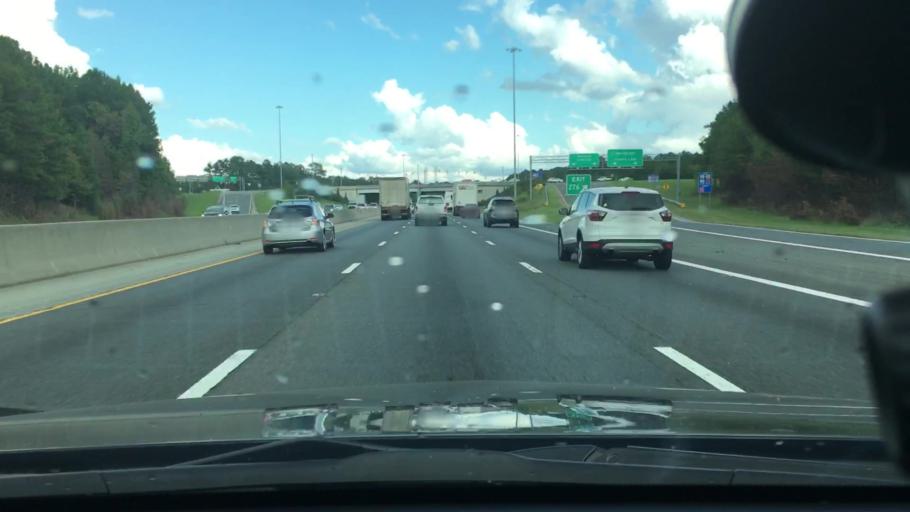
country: US
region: North Carolina
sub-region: Durham County
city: Durham
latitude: 35.9080
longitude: -78.9397
